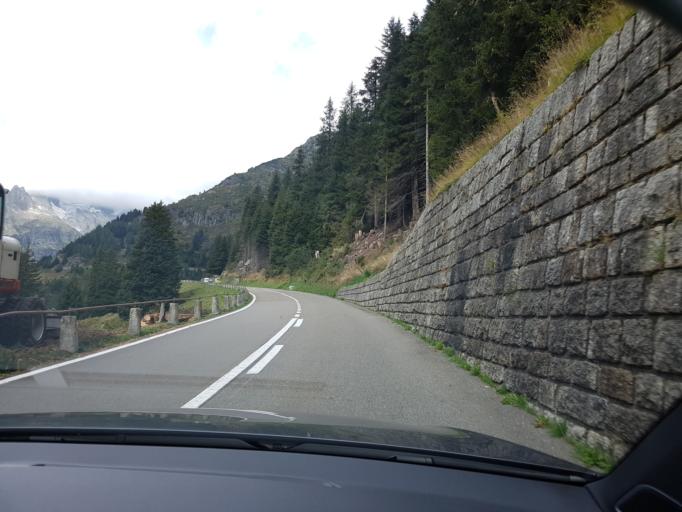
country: CH
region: Uri
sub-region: Uri
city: Andermatt
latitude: 46.7385
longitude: 8.5163
